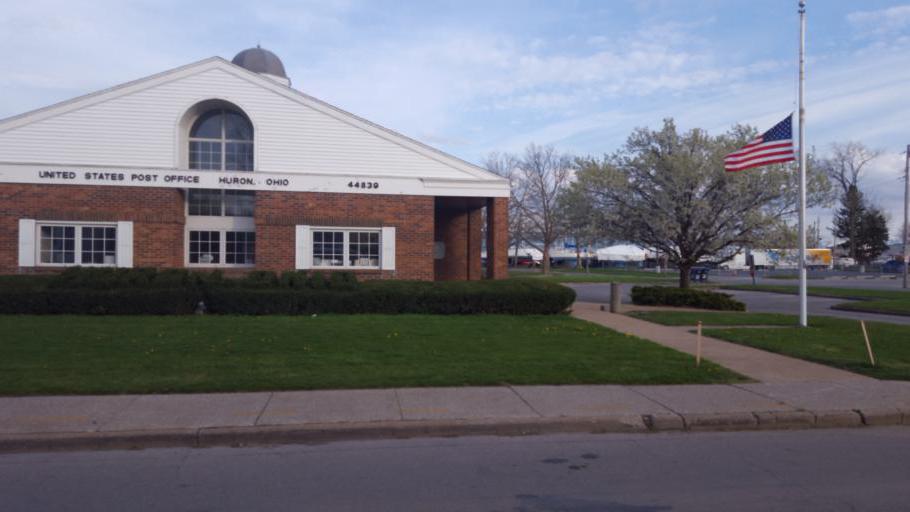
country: US
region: Ohio
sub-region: Erie County
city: Huron
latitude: 41.3930
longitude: -82.5561
